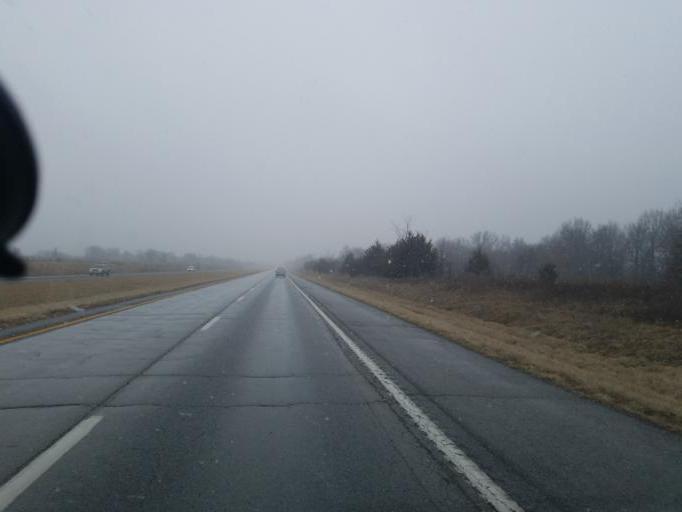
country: US
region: Missouri
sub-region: Macon County
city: La Plata
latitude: 39.9774
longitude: -92.4762
